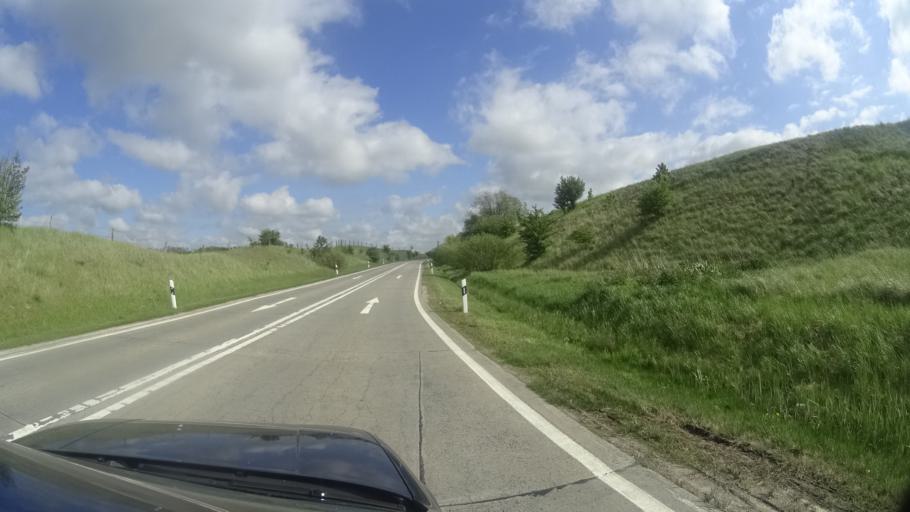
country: DE
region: Mecklenburg-Vorpommern
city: Roggentin
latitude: 54.0504
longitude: 12.2001
